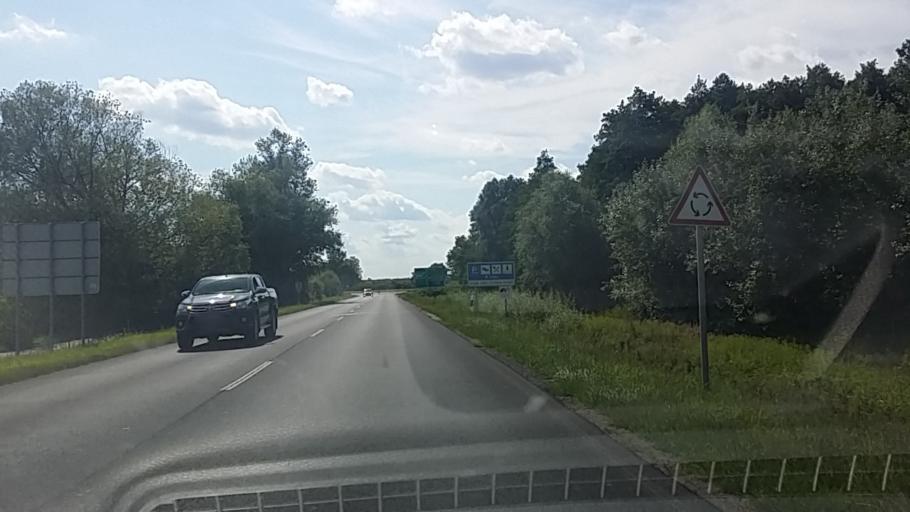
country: HU
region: Zala
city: Nagykanizsa
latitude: 46.4669
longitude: 16.9727
